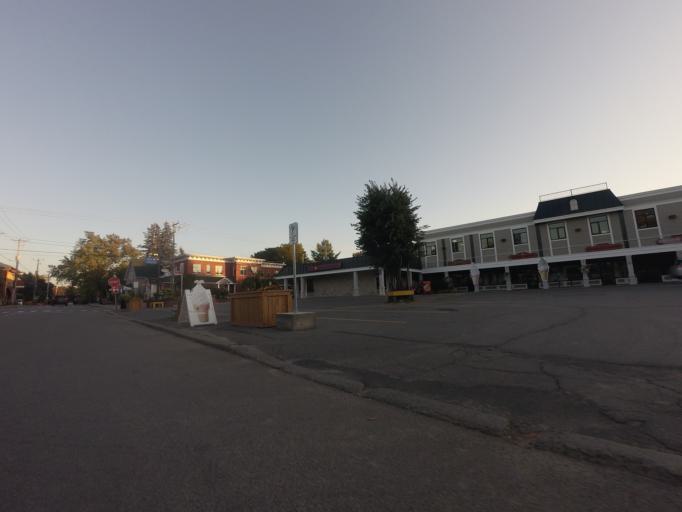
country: CA
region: Quebec
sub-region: Monteregie
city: Hudson
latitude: 45.4582
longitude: -74.1402
